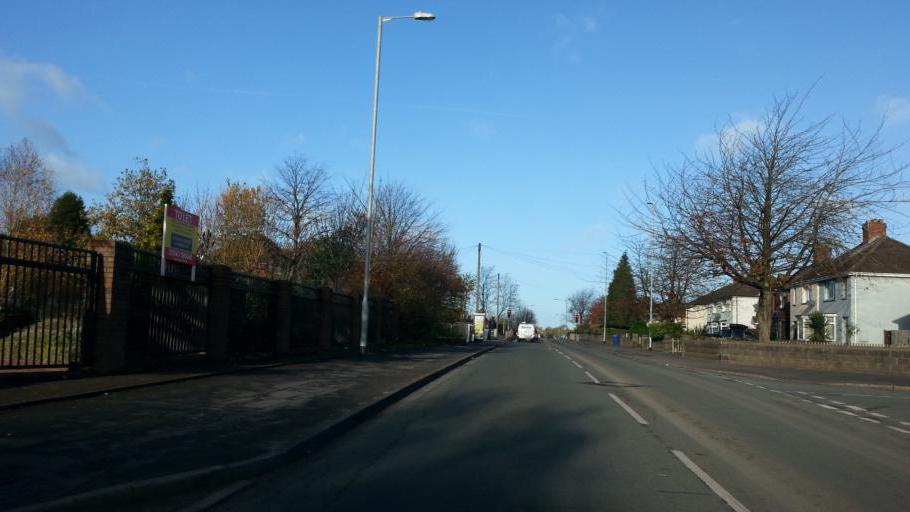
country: GB
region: England
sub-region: Staffordshire
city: Cannock
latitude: 52.6801
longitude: -2.0347
